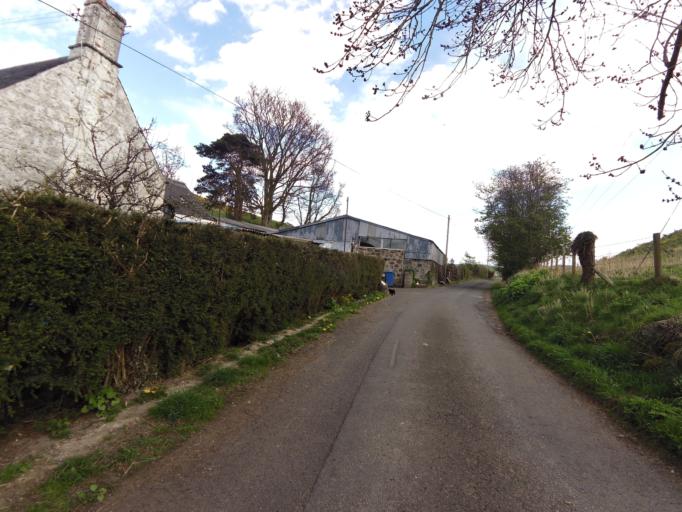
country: GB
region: Scotland
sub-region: Fife
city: Newburgh
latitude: 56.3365
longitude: -3.2492
